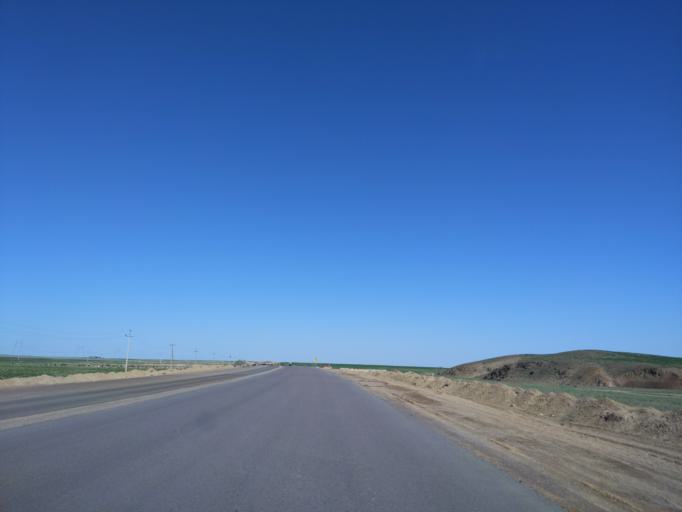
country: KZ
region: Almaty Oblysy
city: Bakanas
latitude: 44.0933
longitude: 75.9888
